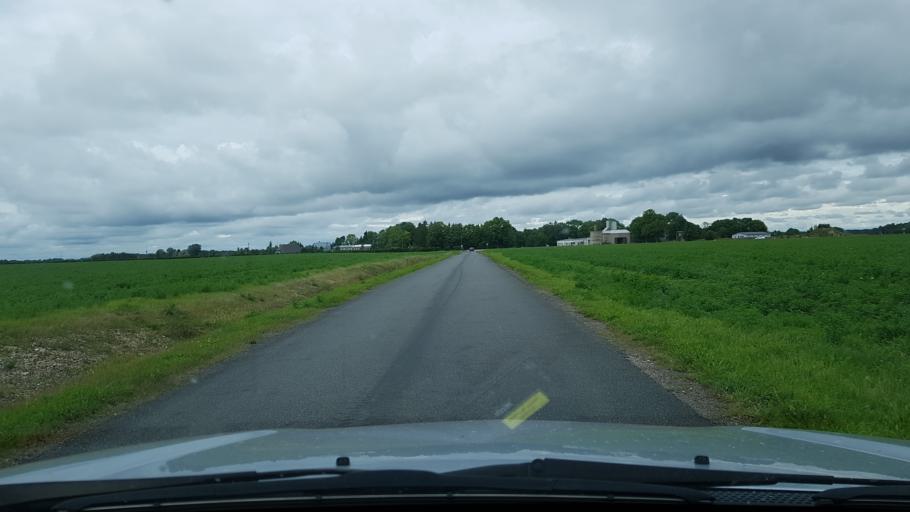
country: EE
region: Harju
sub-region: Rae vald
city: Vaida
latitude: 59.3578
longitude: 24.9651
